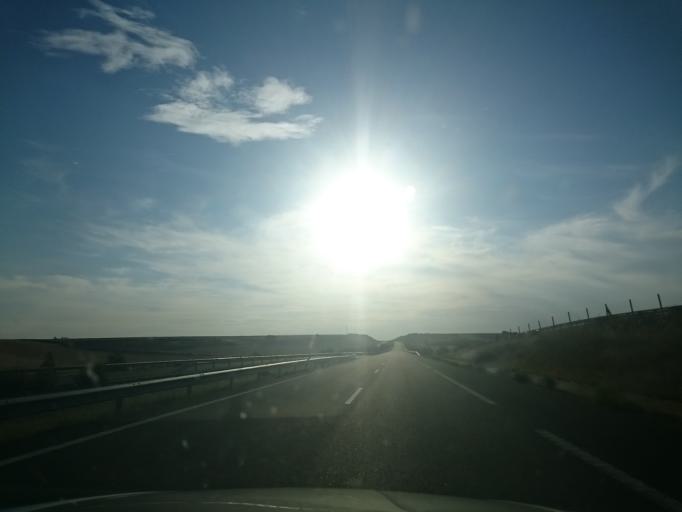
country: ES
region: Castille and Leon
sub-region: Provincia de Palencia
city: Ledigos
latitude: 42.3628
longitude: -4.8494
